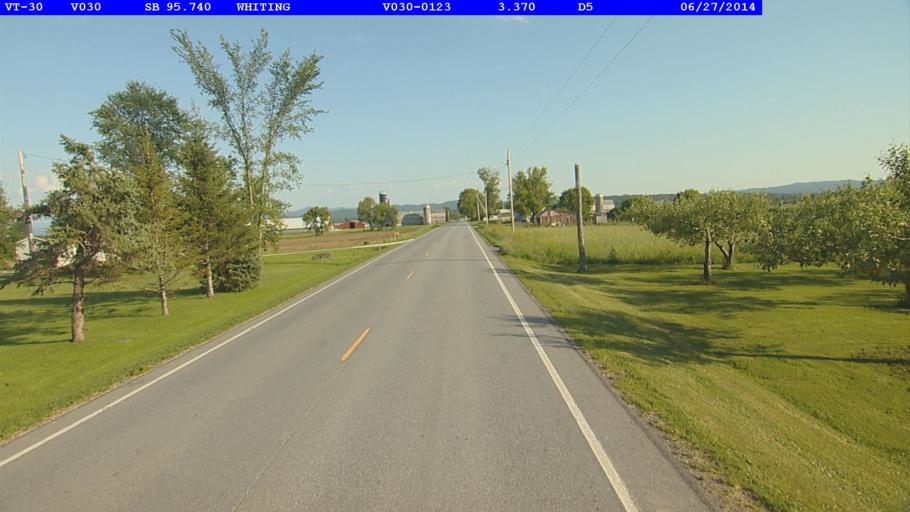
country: US
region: Vermont
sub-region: Addison County
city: Middlebury (village)
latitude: 43.8859
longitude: -73.2013
